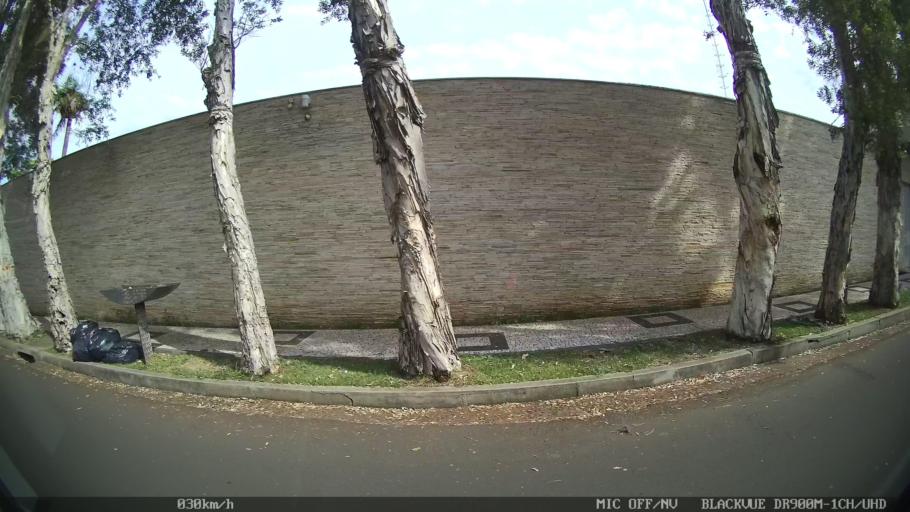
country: BR
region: Sao Paulo
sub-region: Piracicaba
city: Piracicaba
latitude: -22.7224
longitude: -47.6676
